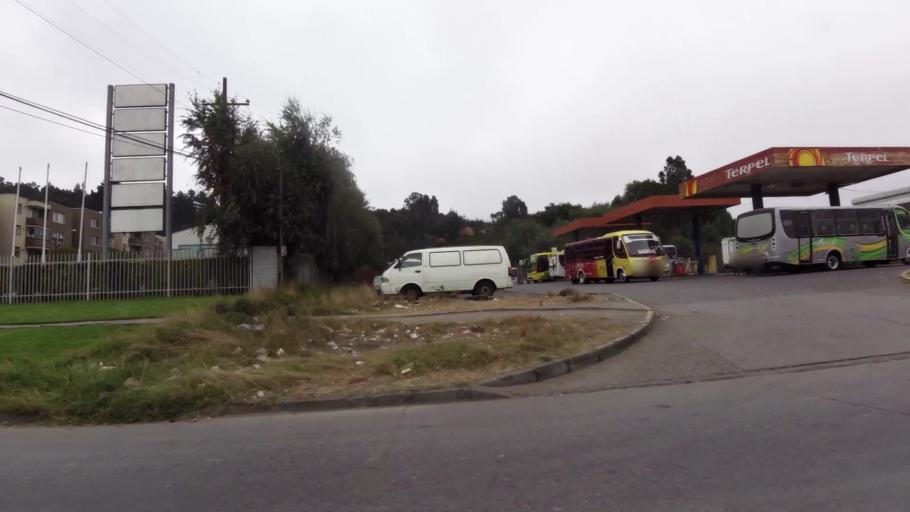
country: CL
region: Biobio
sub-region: Provincia de Concepcion
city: Concepcion
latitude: -36.8219
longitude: -73.0053
